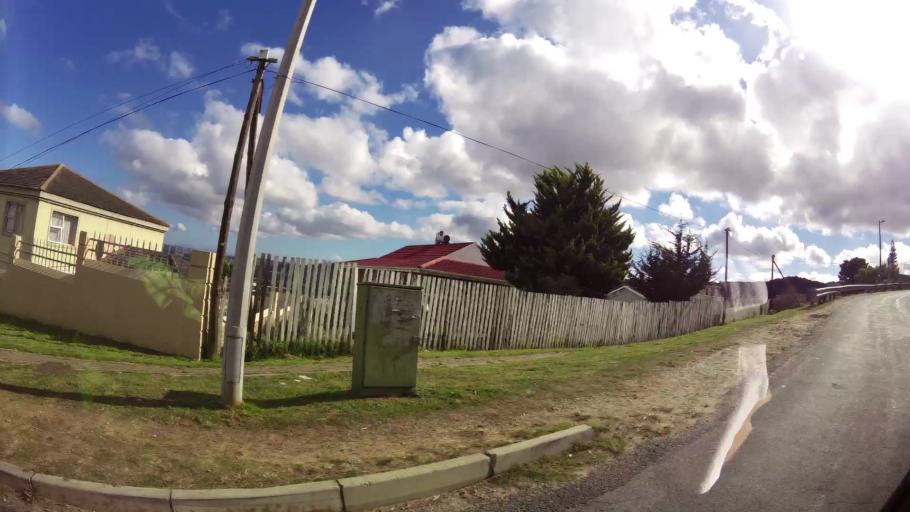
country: ZA
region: Western Cape
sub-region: Eden District Municipality
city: Knysna
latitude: -34.0479
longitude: 23.0831
